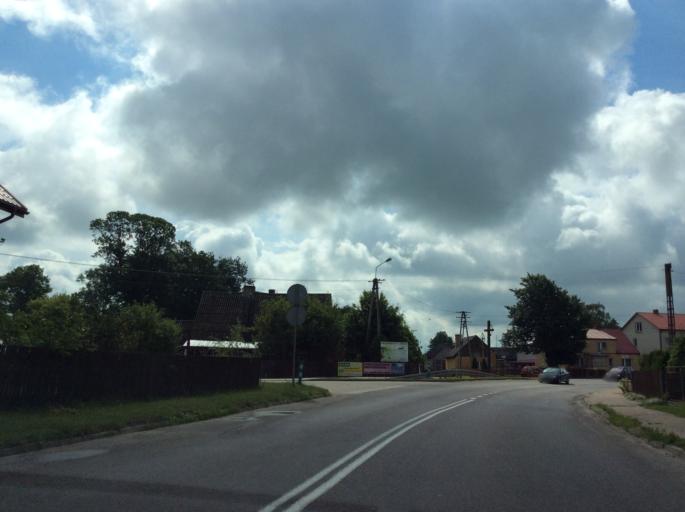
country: PL
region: Warmian-Masurian Voivodeship
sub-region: Powiat szczycienski
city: Rozogi
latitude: 53.4409
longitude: 21.3708
